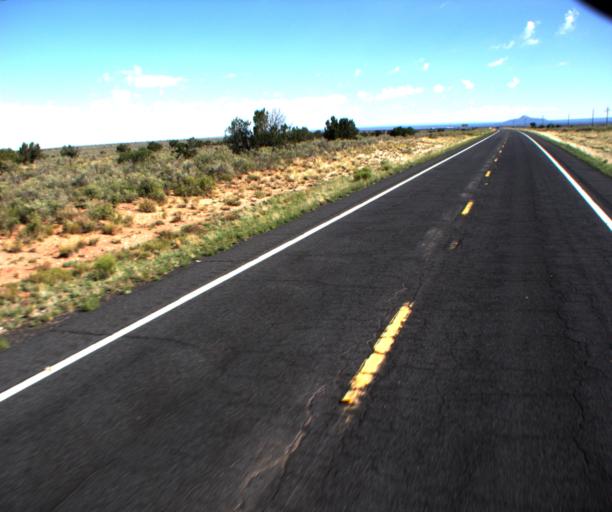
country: US
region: Arizona
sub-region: Coconino County
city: Williams
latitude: 35.6007
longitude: -112.1471
